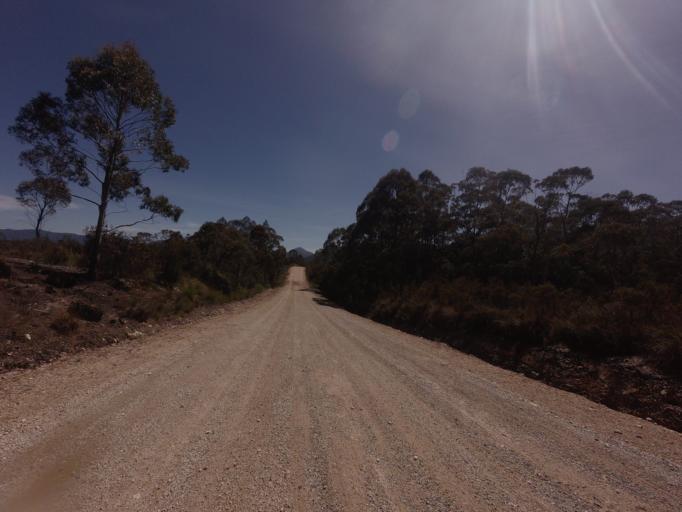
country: AU
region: Tasmania
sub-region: Huon Valley
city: Geeveston
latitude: -42.9665
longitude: 146.3616
